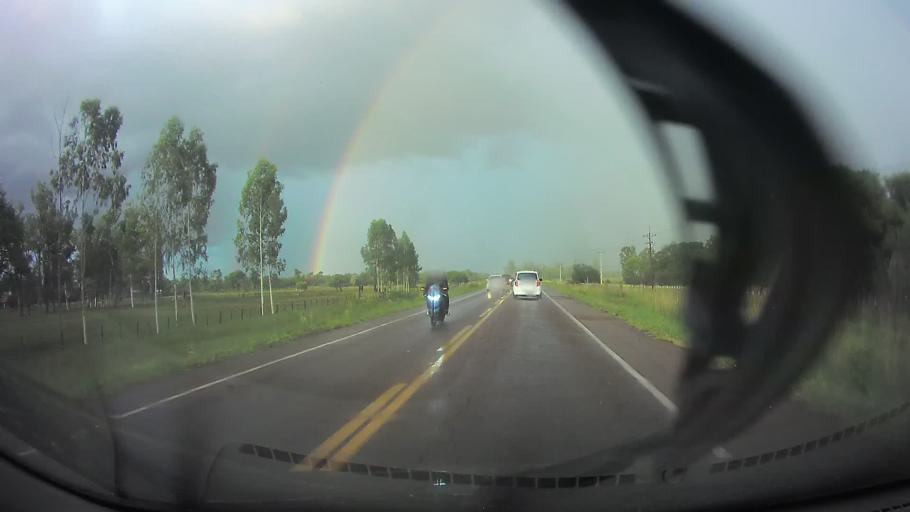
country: PY
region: Paraguari
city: Paraguari
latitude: -25.7103
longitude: -57.1890
